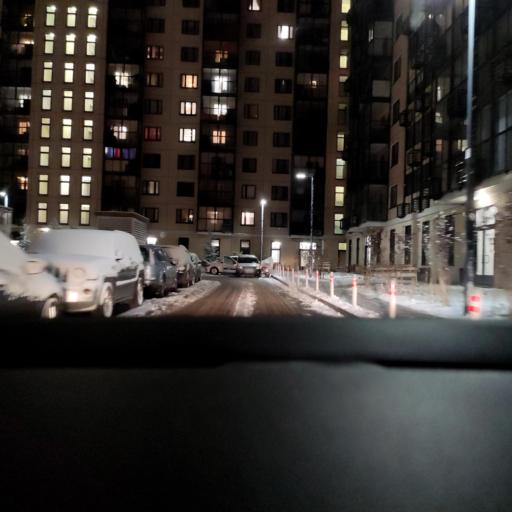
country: RU
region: Moskovskaya
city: Pavshino
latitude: 55.8630
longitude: 37.3734
